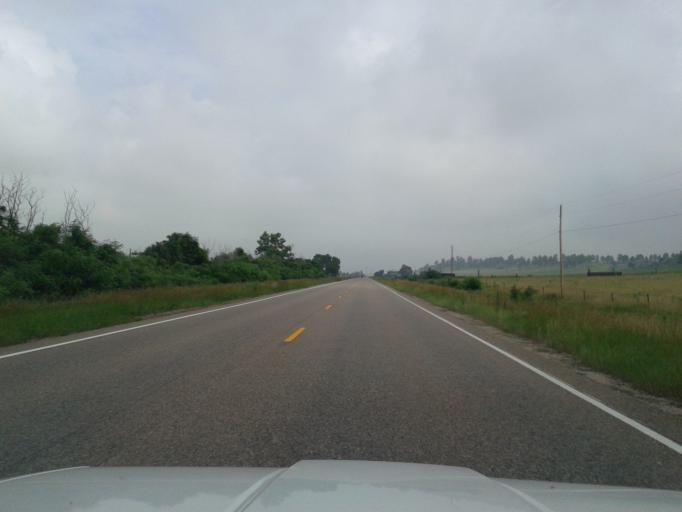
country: US
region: Colorado
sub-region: Elbert County
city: Elizabeth
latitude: 39.2463
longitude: -104.6984
